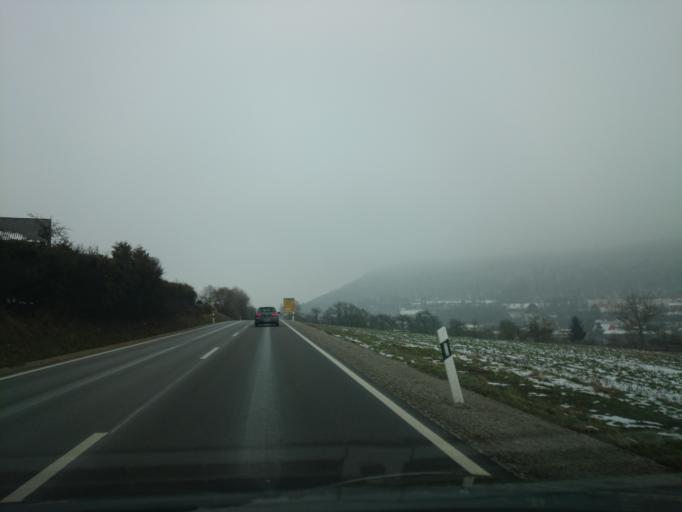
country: DE
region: Bavaria
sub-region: Regierungsbezirk Mittelfranken
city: Greding
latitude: 49.0488
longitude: 11.3448
